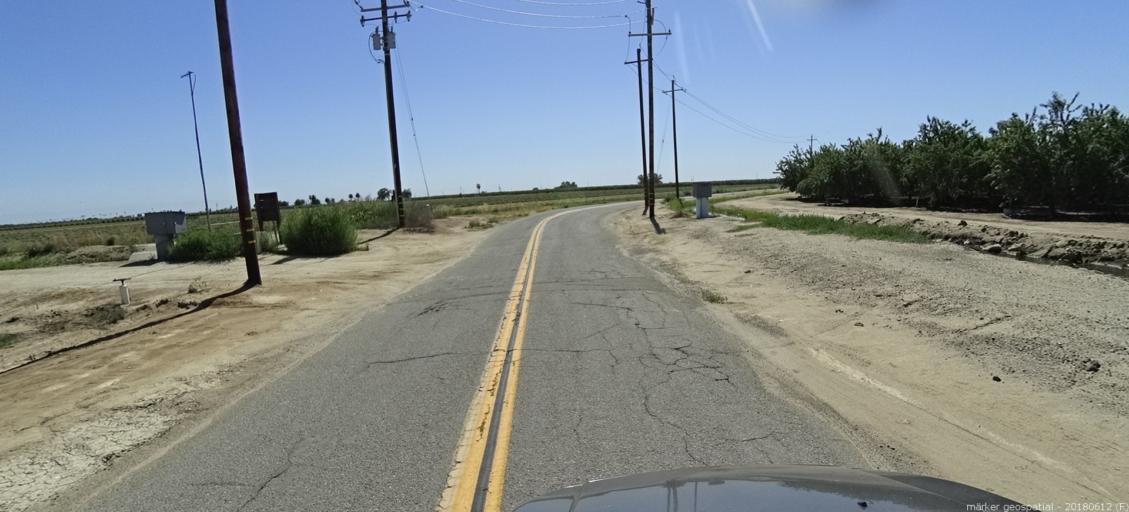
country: US
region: California
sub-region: Madera County
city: Chowchilla
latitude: 37.0326
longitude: -120.3469
